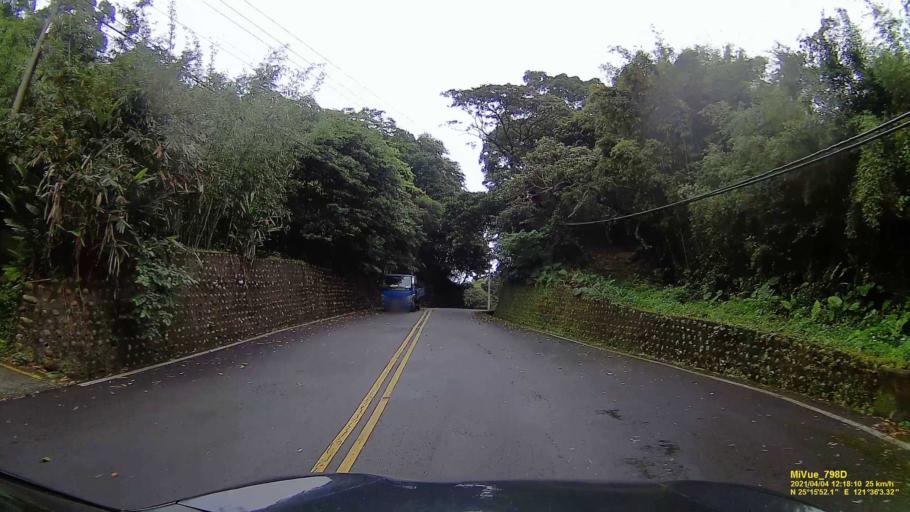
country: TW
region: Taiwan
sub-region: Keelung
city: Keelung
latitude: 25.2645
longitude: 121.6010
